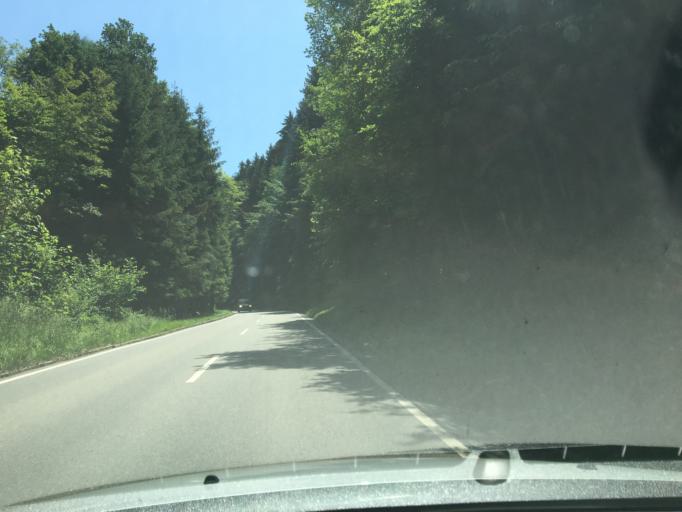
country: DE
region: Bavaria
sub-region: Upper Bavaria
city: Halsbach
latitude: 48.1360
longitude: 12.6482
